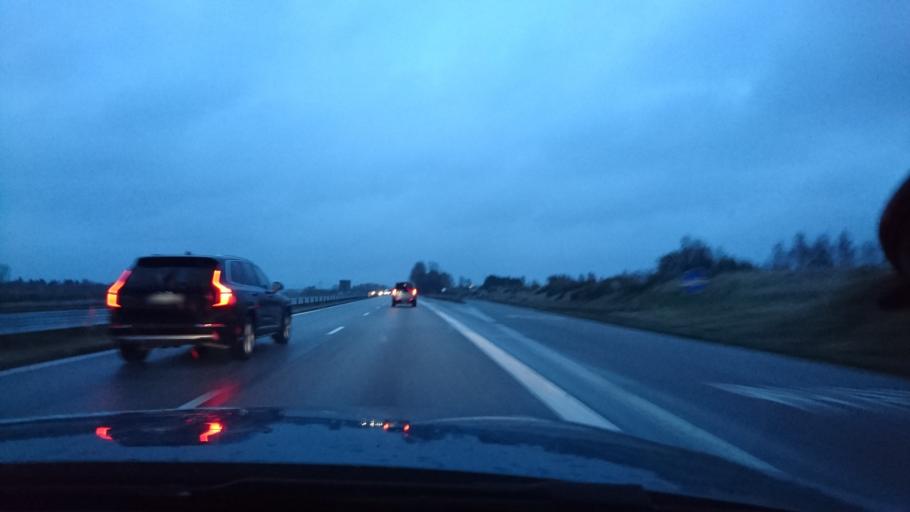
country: SE
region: Skane
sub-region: Helsingborg
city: Hyllinge
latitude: 56.1033
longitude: 12.8549
